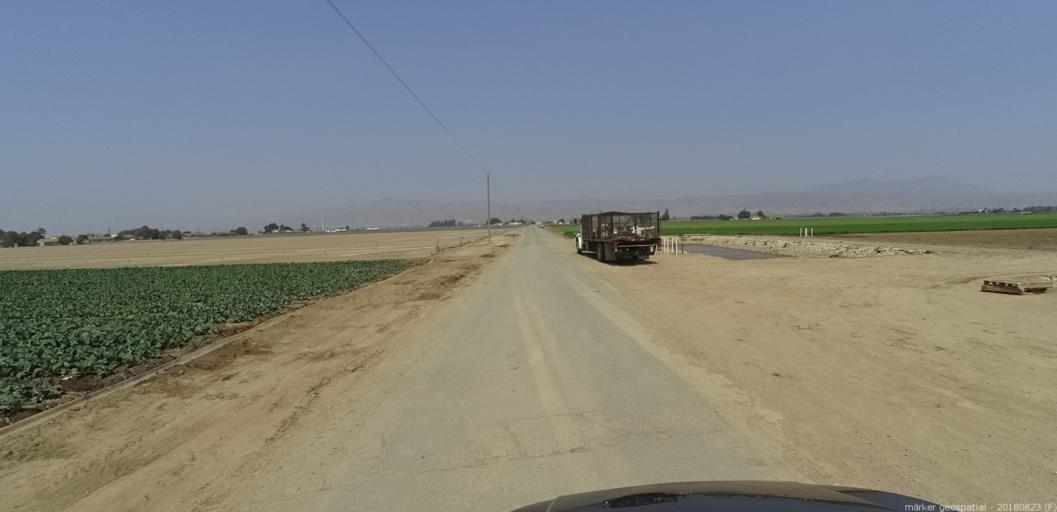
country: US
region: California
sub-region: Monterey County
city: Soledad
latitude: 36.3946
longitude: -121.3453
